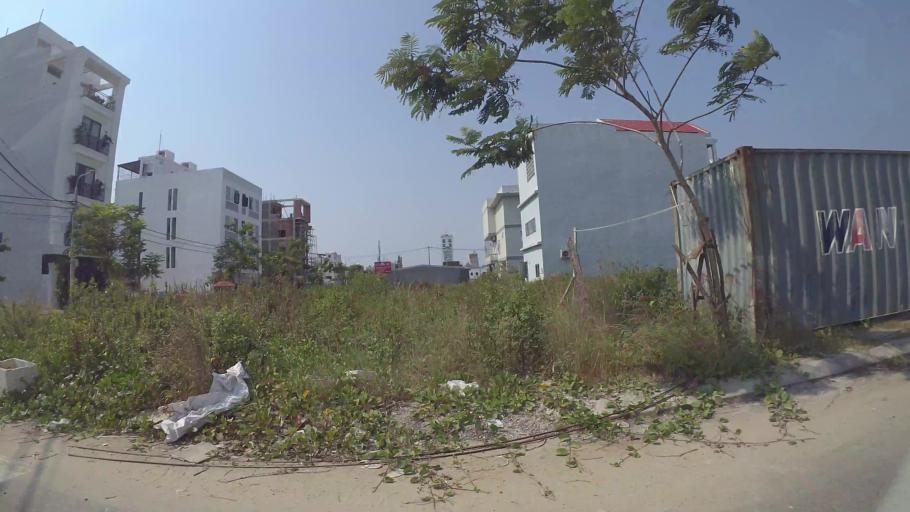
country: VN
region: Da Nang
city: Ngu Hanh Son
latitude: 16.0365
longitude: 108.2455
